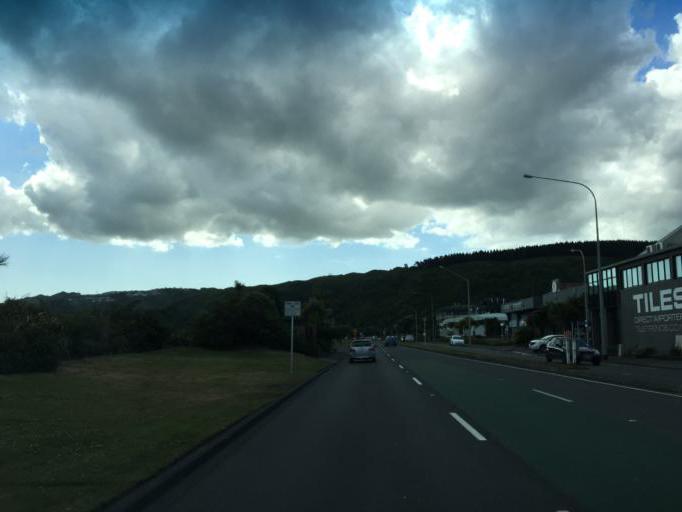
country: NZ
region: Wellington
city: Petone
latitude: -41.2258
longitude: 174.8676
